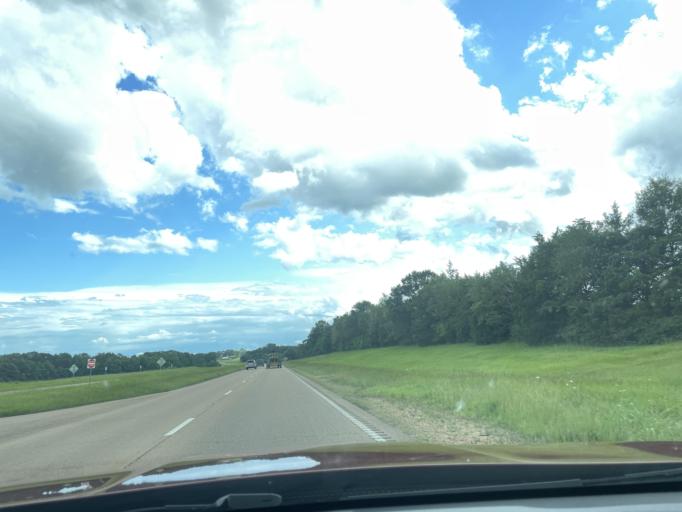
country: US
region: Mississippi
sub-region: Madison County
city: Flora
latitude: 32.5490
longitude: -90.3215
